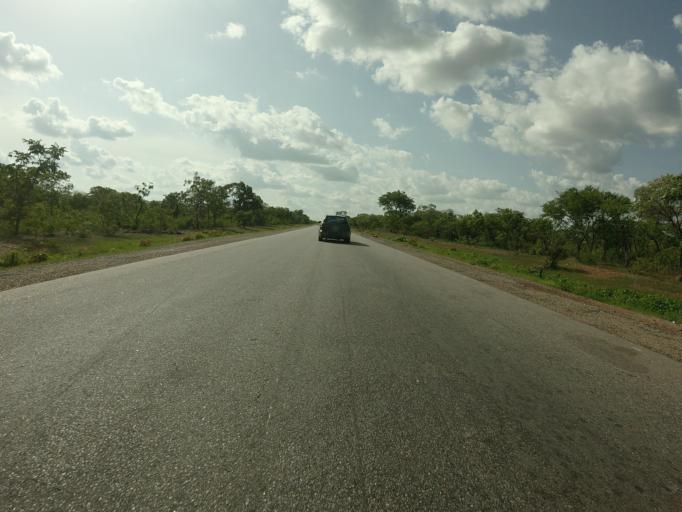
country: GH
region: Upper East
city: Bolgatanga
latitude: 10.5261
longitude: -0.8156
